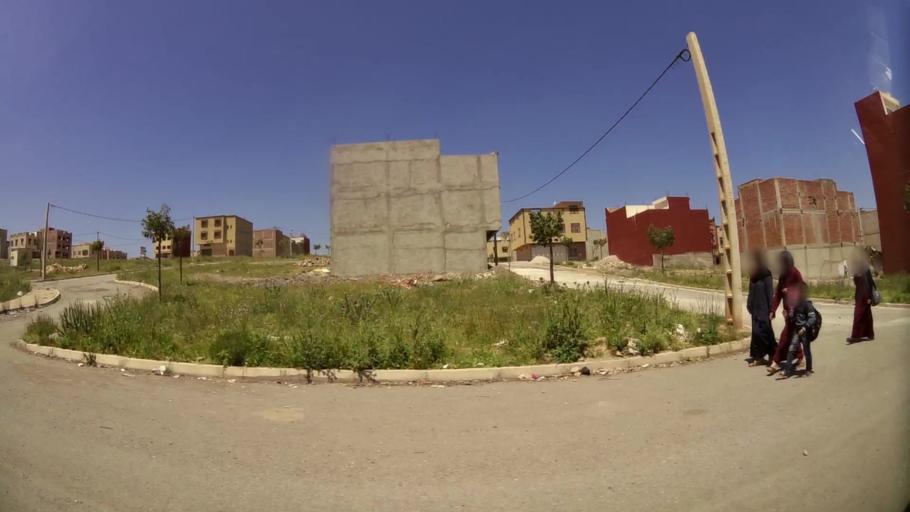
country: MA
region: Oriental
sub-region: Oujda-Angad
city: Oujda
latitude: 34.6777
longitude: -1.9508
